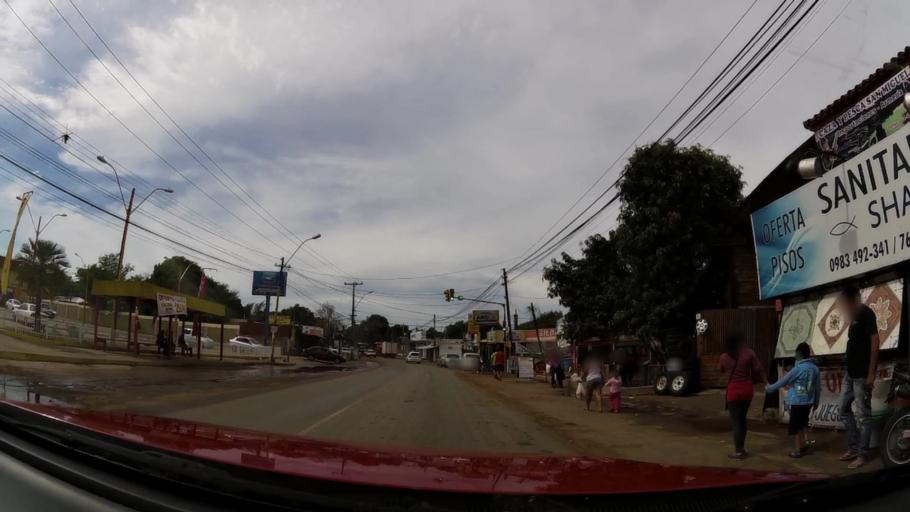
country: PY
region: Central
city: Limpio
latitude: -25.1729
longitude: -57.4726
